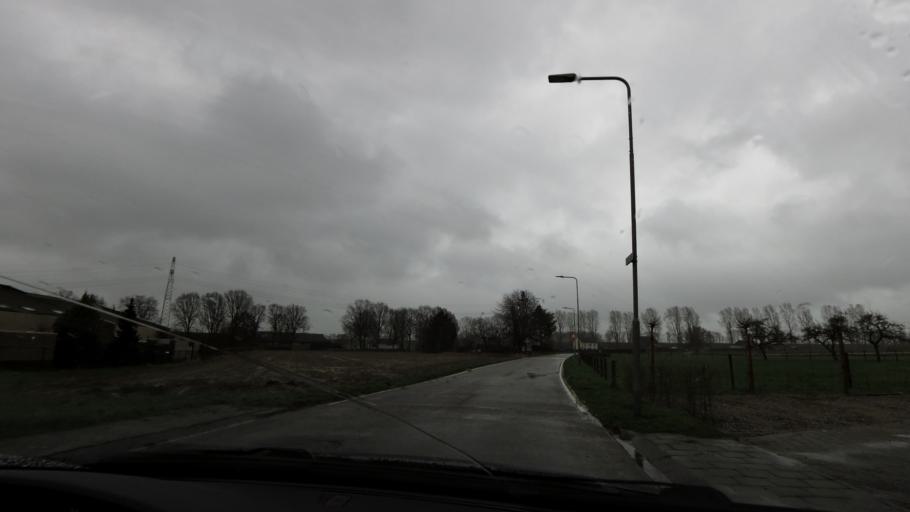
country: NL
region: Limburg
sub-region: Gemeente Sittard-Geleen
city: Born
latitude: 51.0274
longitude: 5.7863
